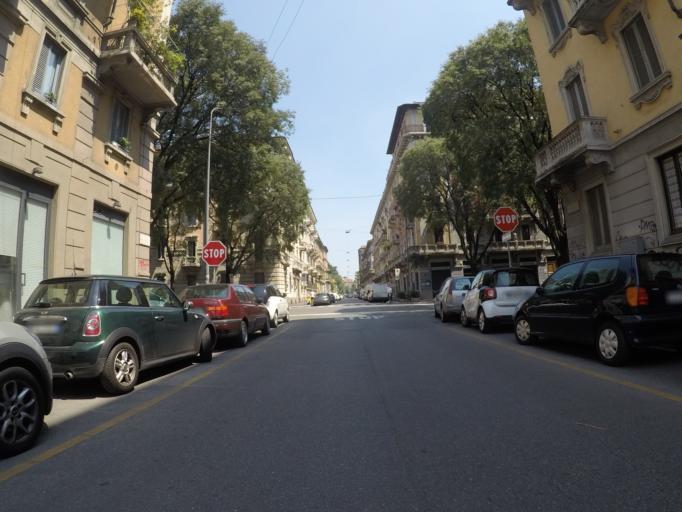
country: IT
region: Lombardy
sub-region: Citta metropolitana di Milano
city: Milano
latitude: 45.4693
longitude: 9.2144
